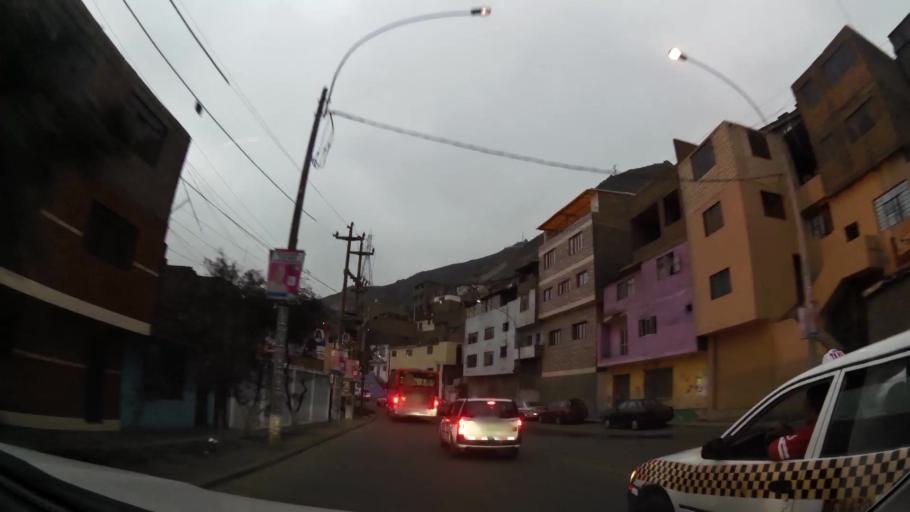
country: PE
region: Lima
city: Lima
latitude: -12.0345
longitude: -77.0131
